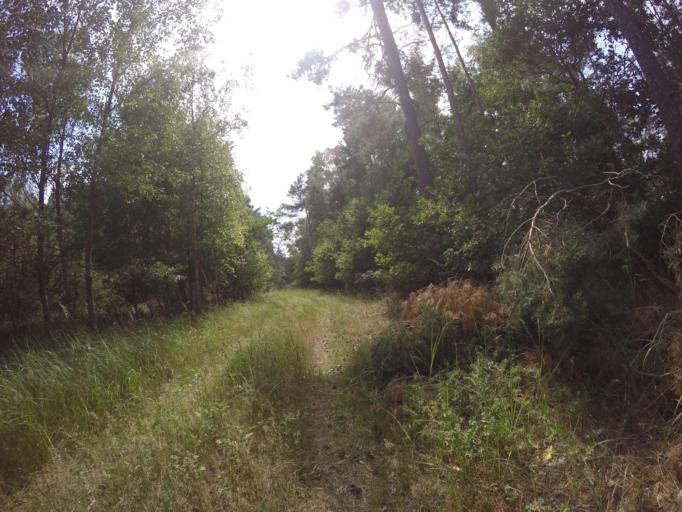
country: DE
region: Lower Saxony
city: Bleckede
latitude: 53.2547
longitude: 10.7243
